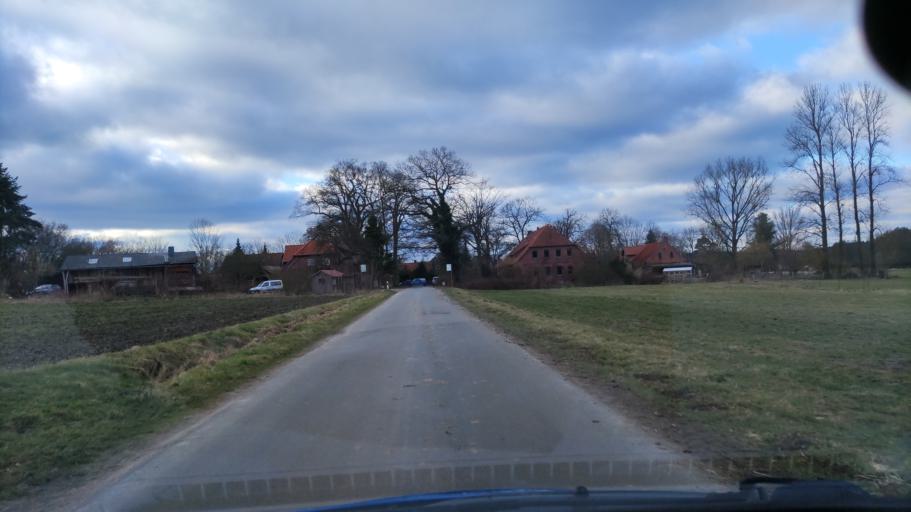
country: DE
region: Lower Saxony
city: Gohrde
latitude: 53.1573
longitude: 10.8824
